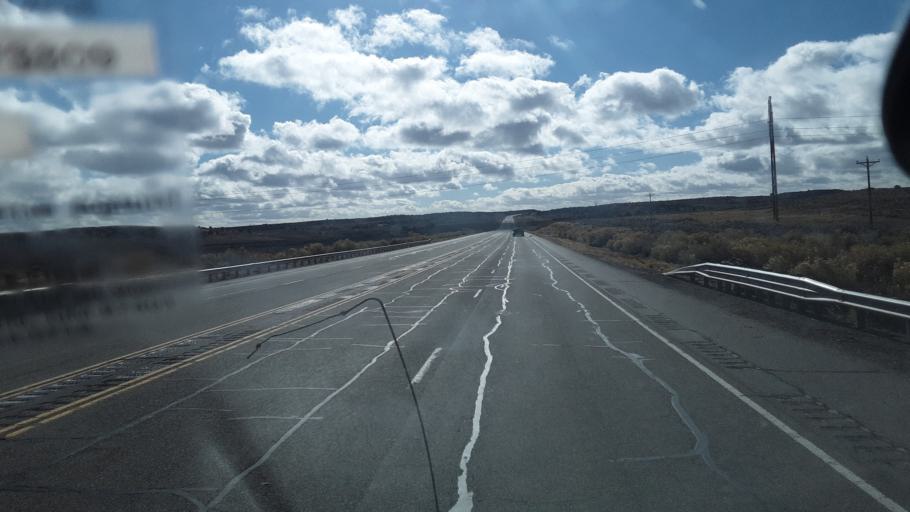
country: US
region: New Mexico
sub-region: San Juan County
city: Bloomfield
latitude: 36.3438
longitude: -107.7935
